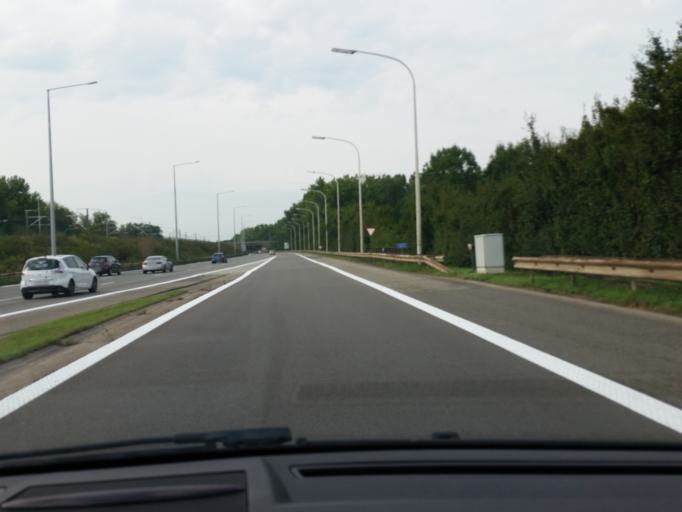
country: BE
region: Flanders
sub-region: Provincie Vlaams-Brabant
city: Zemst
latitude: 50.9785
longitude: 4.4881
